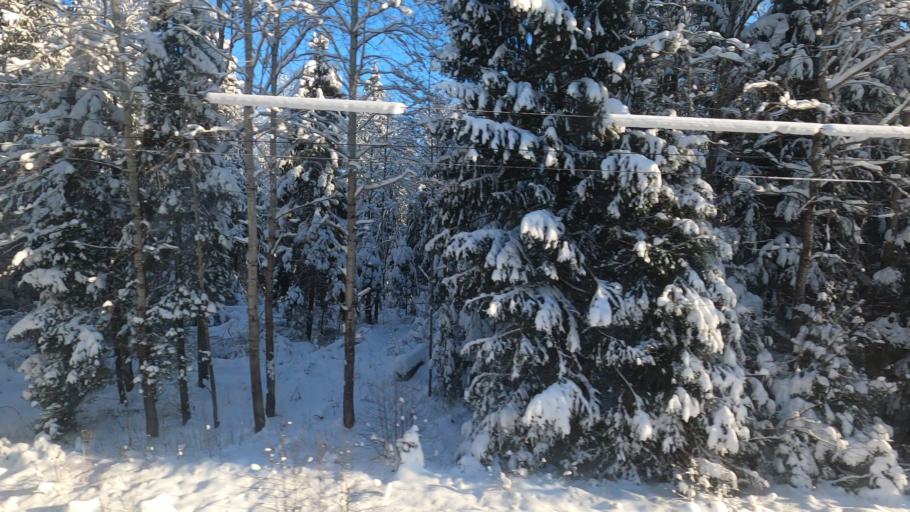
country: RU
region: Moskovskaya
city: Zhukovka
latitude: 56.4953
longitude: 37.5518
